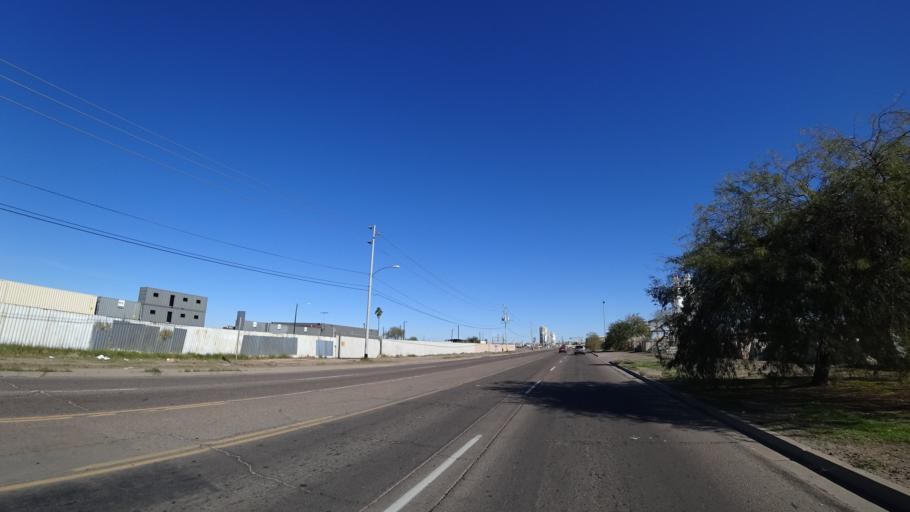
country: US
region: Arizona
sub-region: Maricopa County
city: Phoenix
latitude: 33.4222
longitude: -112.1038
